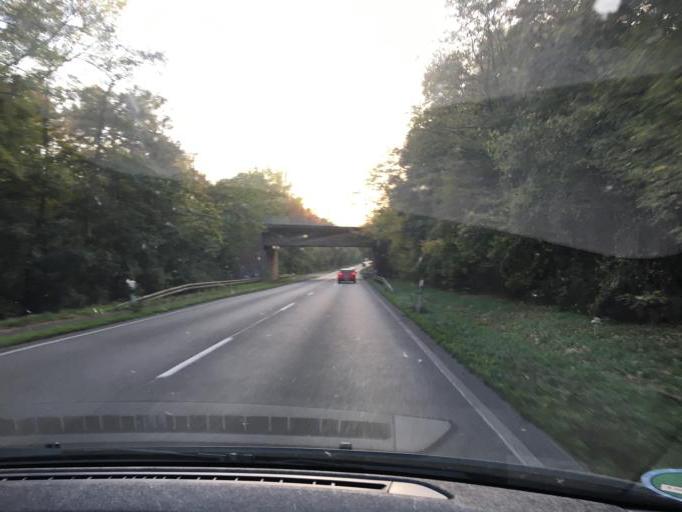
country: DE
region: North Rhine-Westphalia
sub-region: Regierungsbezirk Koln
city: Hurth
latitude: 50.8613
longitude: 6.8172
